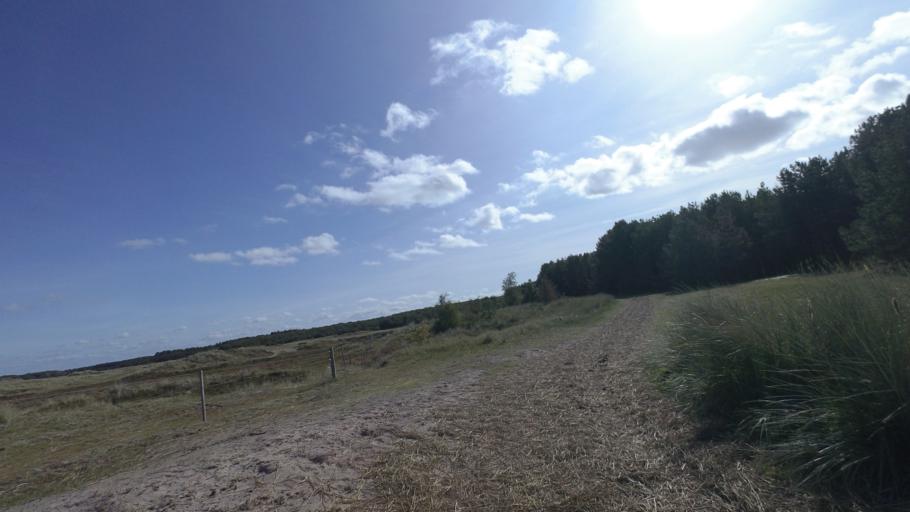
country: NL
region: Friesland
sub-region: Gemeente Ameland
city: Hollum
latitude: 53.4533
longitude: 5.6963
